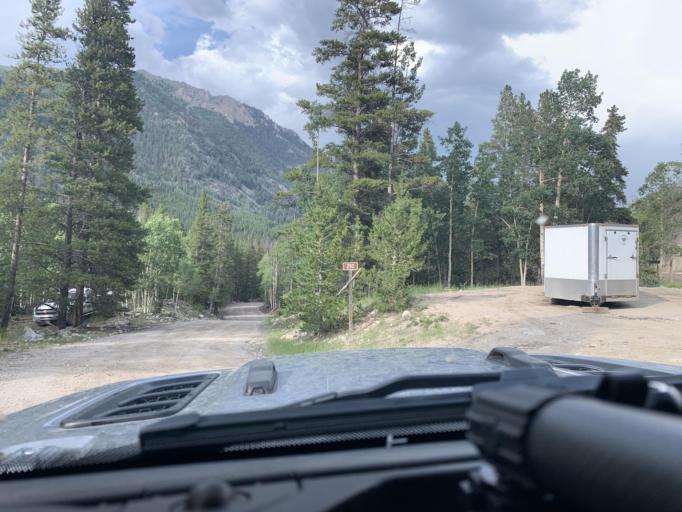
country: US
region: Colorado
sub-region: Chaffee County
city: Buena Vista
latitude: 38.7056
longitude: -106.3422
